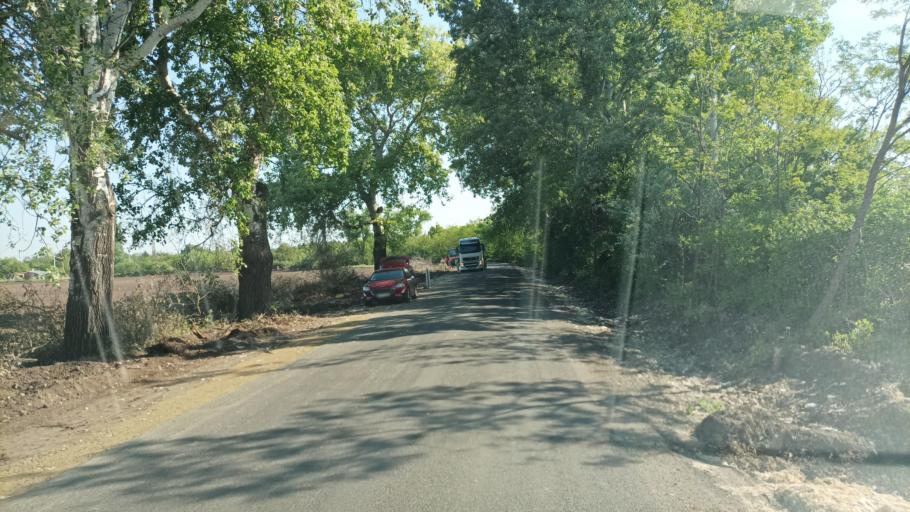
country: HU
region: Pest
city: Nyaregyhaza
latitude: 47.3015
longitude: 19.5026
